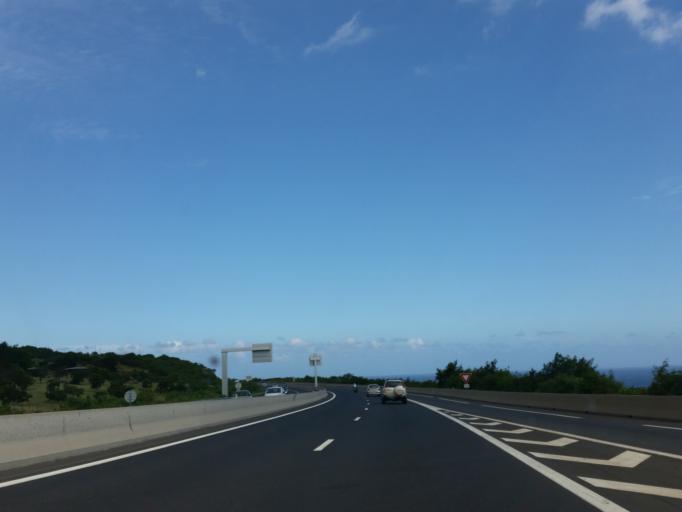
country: RE
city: Piton Saint-Leu
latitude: -21.2015
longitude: 55.2930
